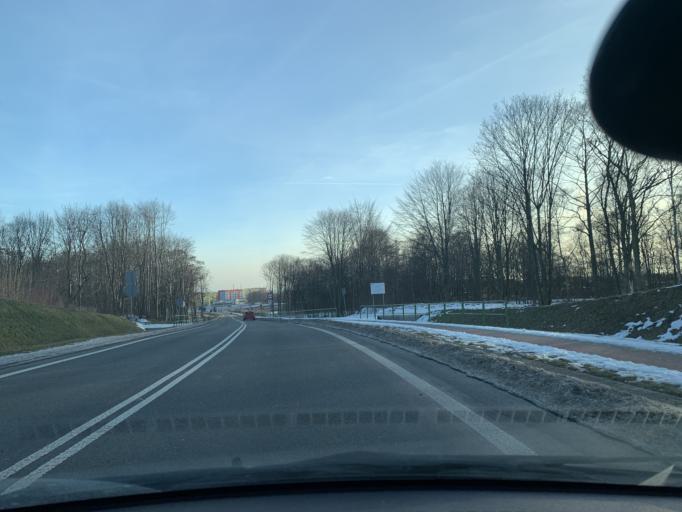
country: PL
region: Silesian Voivodeship
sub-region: Powiat tarnogorski
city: Radzionkow
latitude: 50.4044
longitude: 18.8913
